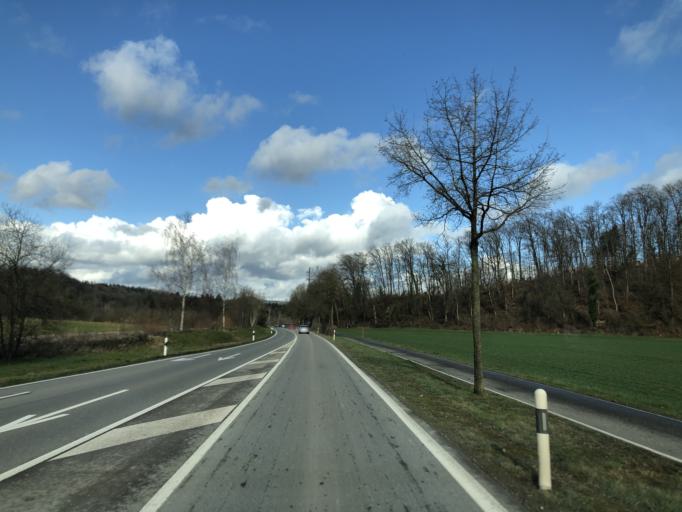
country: CH
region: Aargau
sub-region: Bezirk Baden
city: Birmenstorf
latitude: 47.4658
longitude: 8.2392
